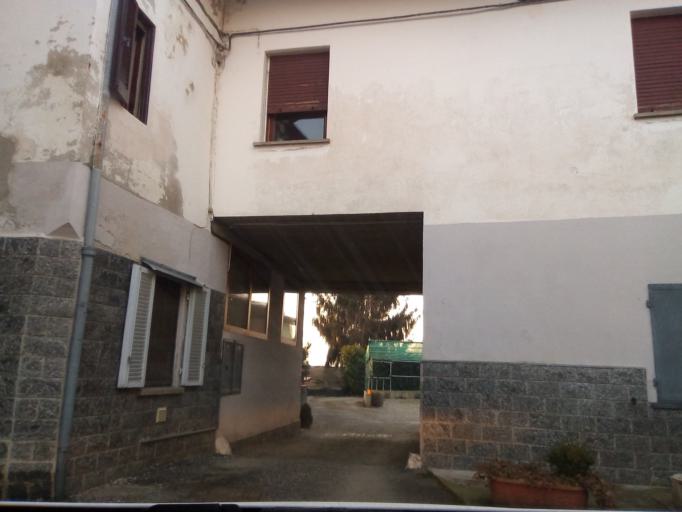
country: IT
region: Piedmont
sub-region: Provincia di Torino
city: Pavone Canavese
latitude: 45.4292
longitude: 7.8796
